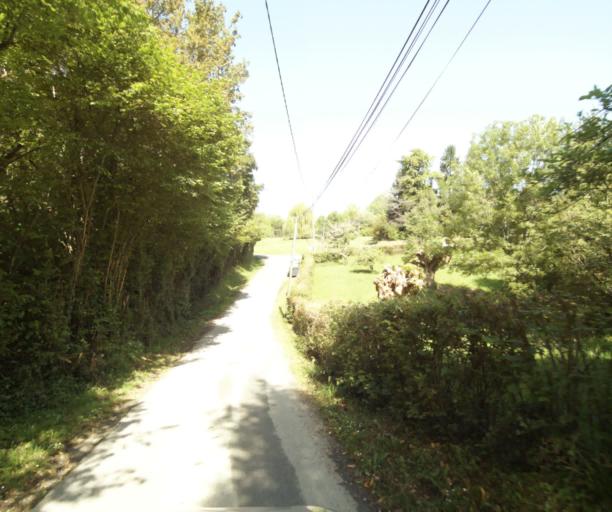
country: FR
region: Aquitaine
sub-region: Departement des Pyrenees-Atlantiques
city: Villefranque
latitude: 43.4619
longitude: -1.4460
